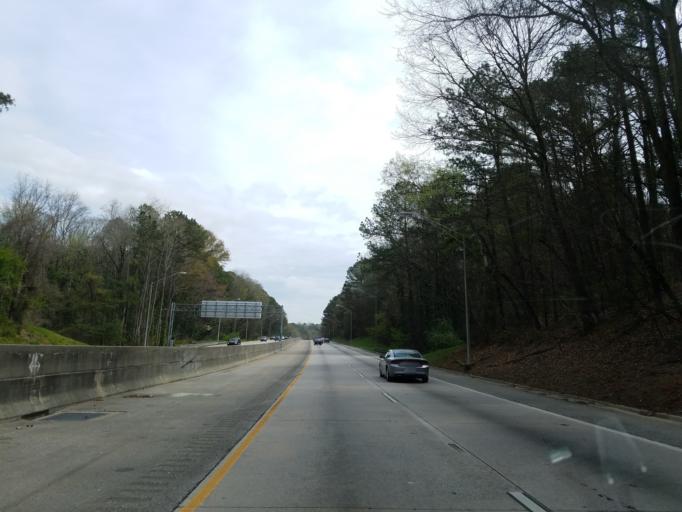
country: US
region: Georgia
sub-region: Fulton County
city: East Point
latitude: 33.6977
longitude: -84.4748
